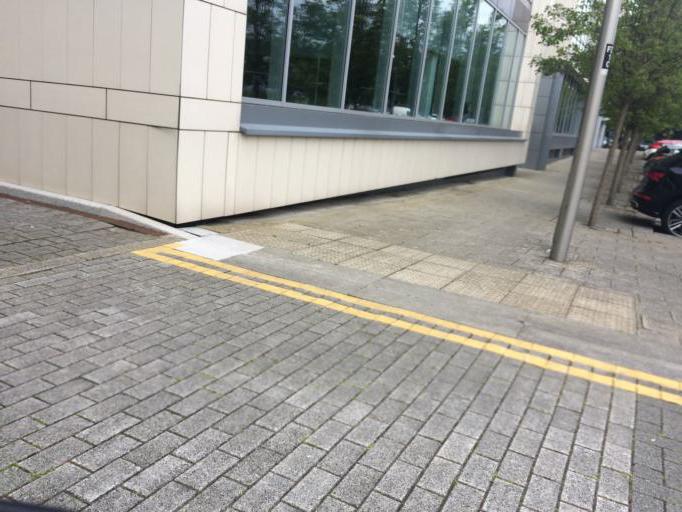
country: GB
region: England
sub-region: Milton Keynes
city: Milton Keynes
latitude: 52.0363
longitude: -0.7667
